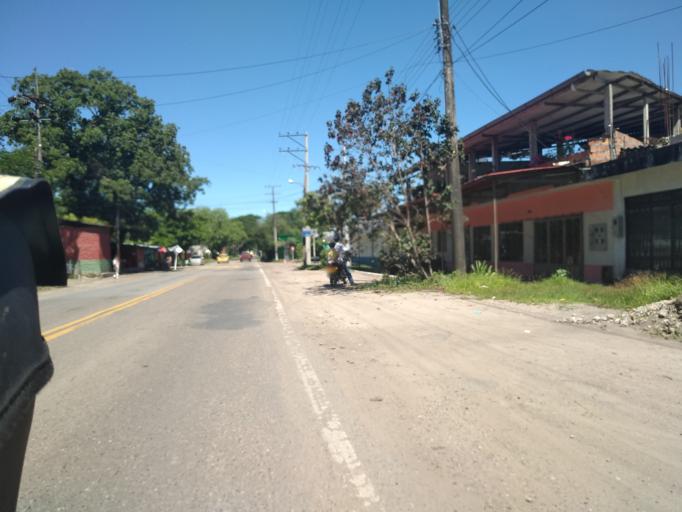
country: CO
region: Cundinamarca
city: Puerto Salgar
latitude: 5.4669
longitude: -74.6532
